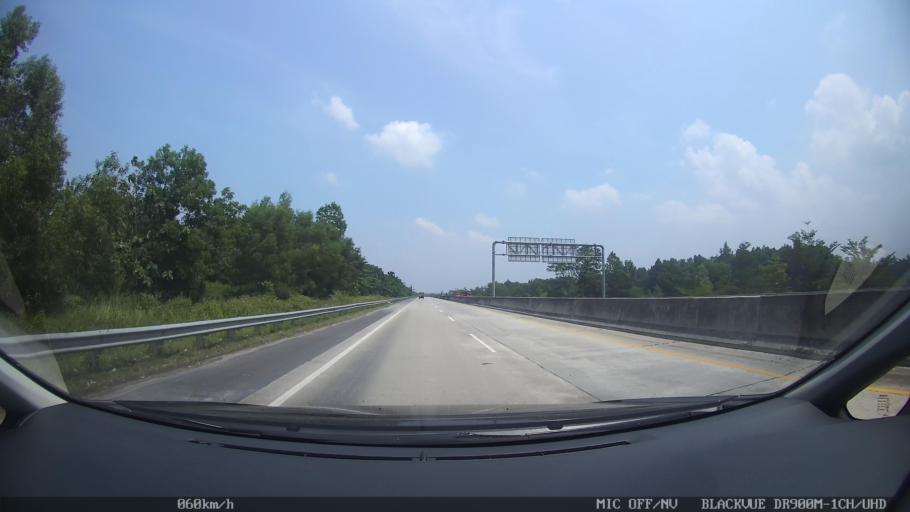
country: ID
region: Lampung
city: Kedaton
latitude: -5.3833
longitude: 105.3354
